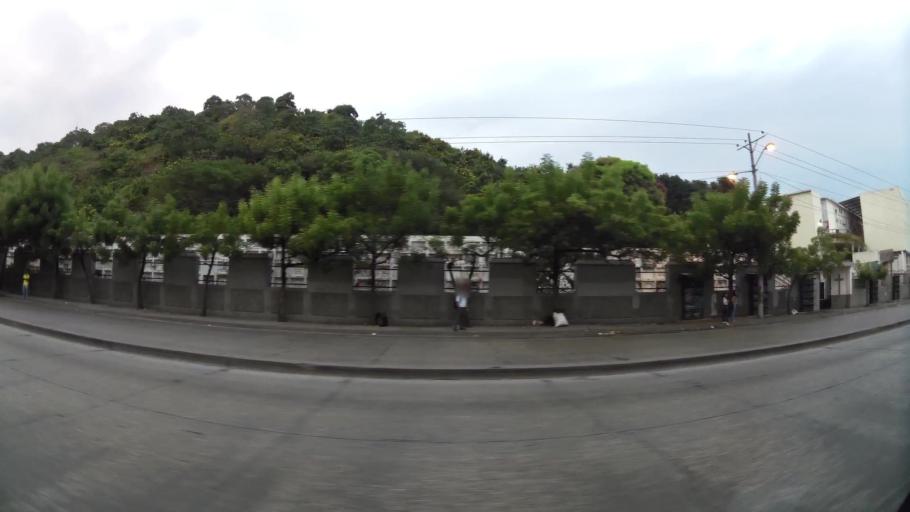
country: EC
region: Guayas
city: Guayaquil
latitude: -2.1803
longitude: -79.8884
